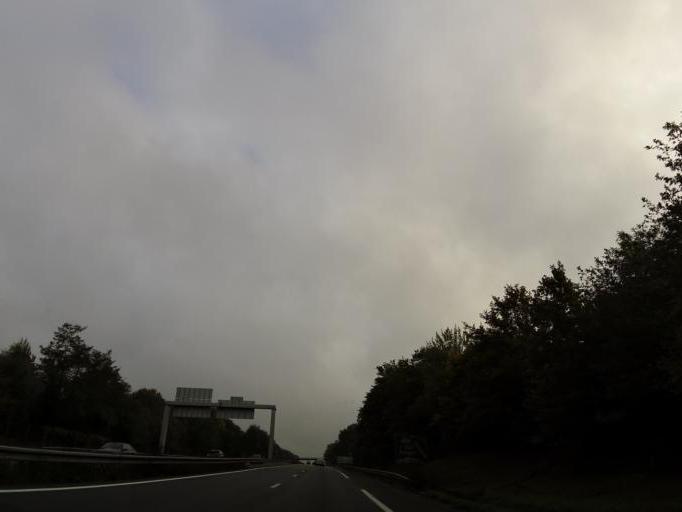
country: FR
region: Ile-de-France
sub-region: Departement de Seine-et-Marne
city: Bouleurs
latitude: 48.8909
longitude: 2.9039
